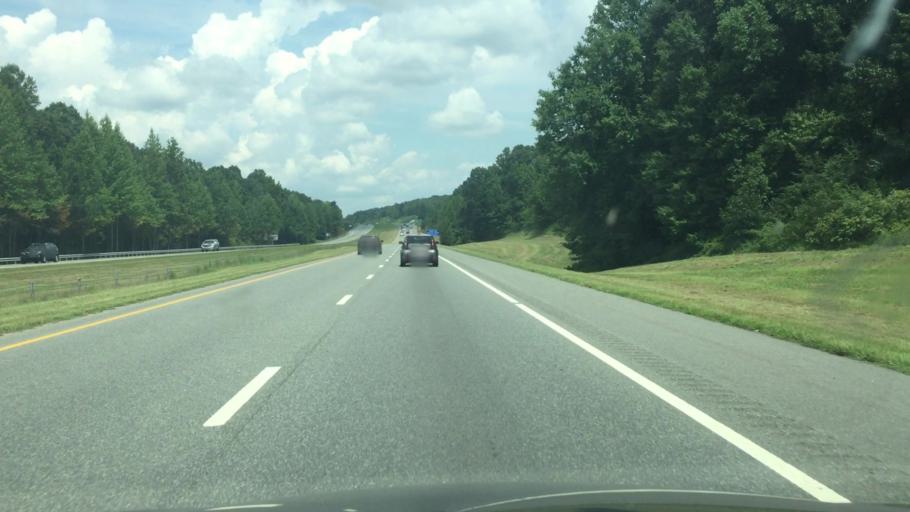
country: US
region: North Carolina
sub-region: Montgomery County
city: Biscoe
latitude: 35.5052
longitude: -79.7811
